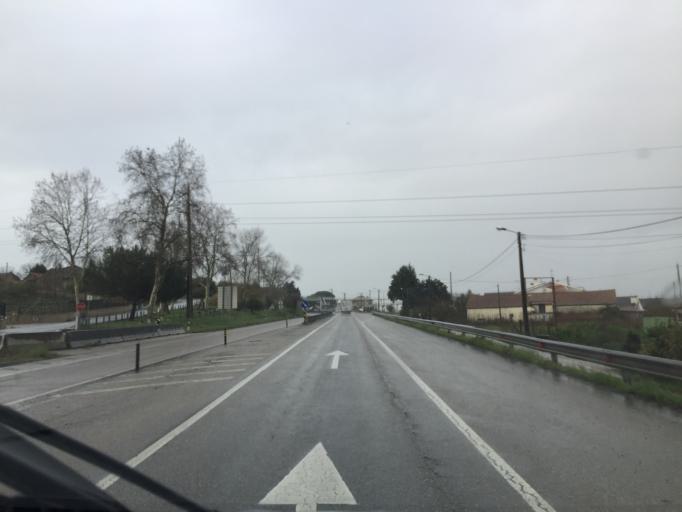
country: PT
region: Leiria
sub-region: Leiria
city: Leiria
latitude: 39.7053
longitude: -8.8276
